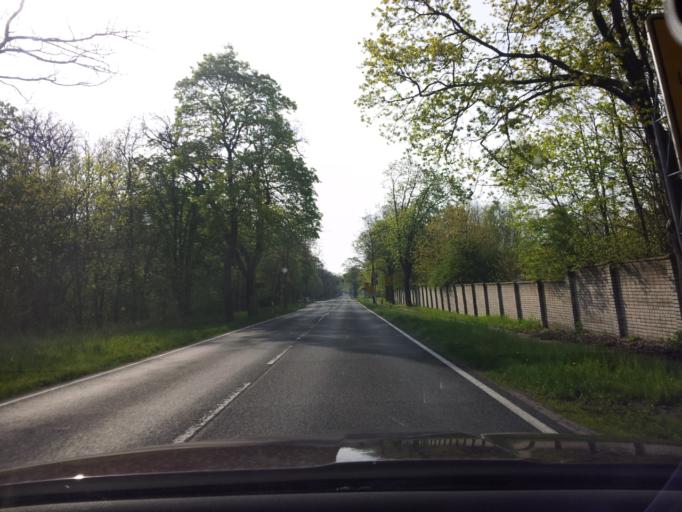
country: DE
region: Brandenburg
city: Niedergorsdorf
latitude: 52.0000
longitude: 13.0298
